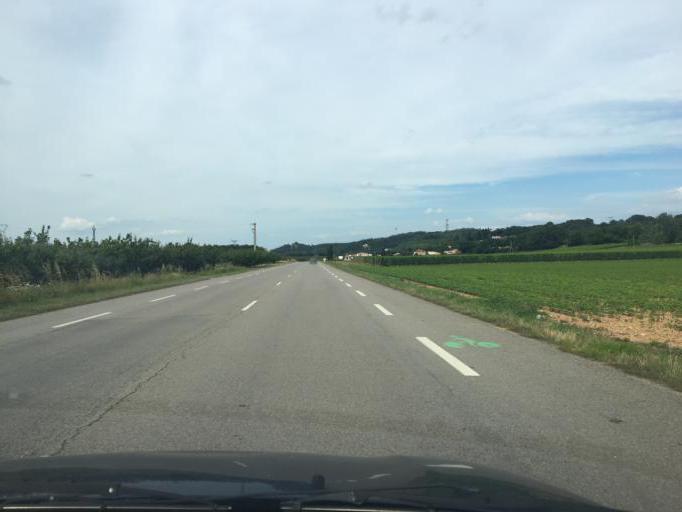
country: FR
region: Rhone-Alpes
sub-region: Departement de la Drome
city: Beaumont-Monteux
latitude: 44.9977
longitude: 4.9168
